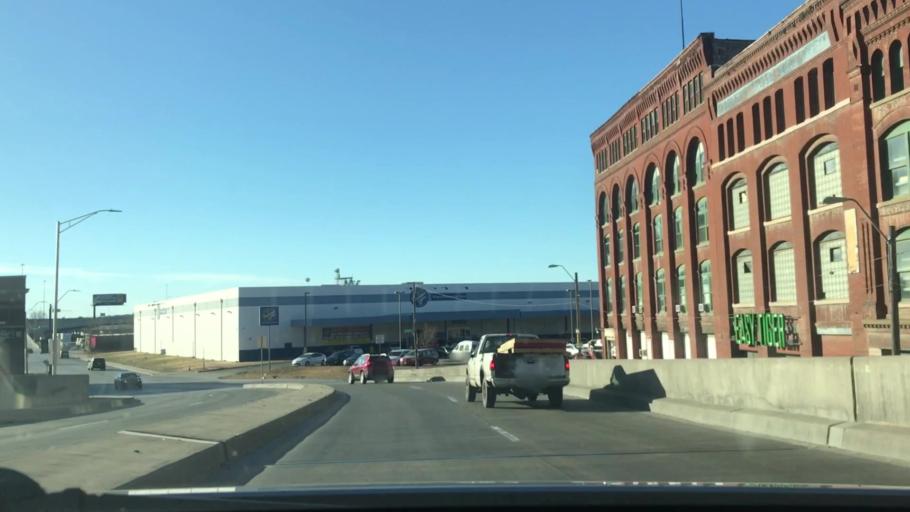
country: US
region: Missouri
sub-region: Jackson County
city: Kansas City
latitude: 39.1007
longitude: -94.6016
